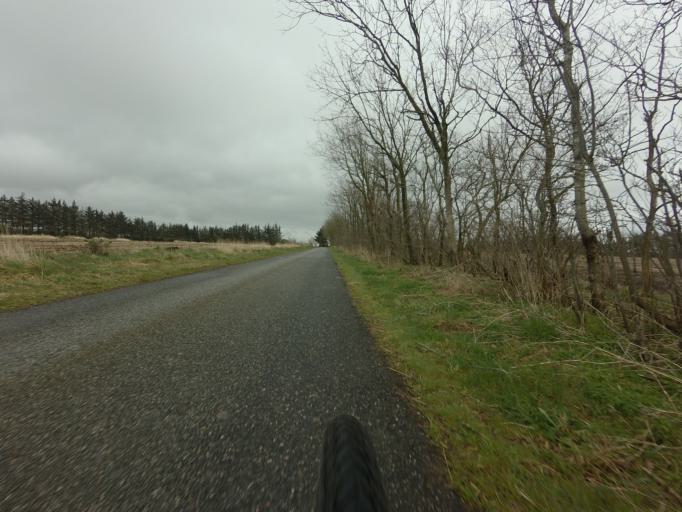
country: DK
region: North Denmark
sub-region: Jammerbugt Kommune
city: Pandrup
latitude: 57.3272
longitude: 9.7862
